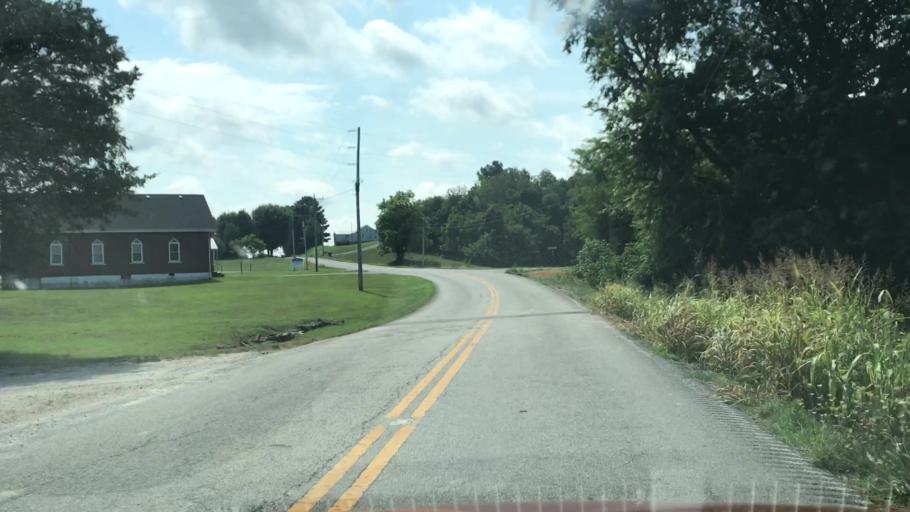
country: US
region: Kentucky
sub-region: Barren County
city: Glasgow
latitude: 36.8417
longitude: -85.8346
